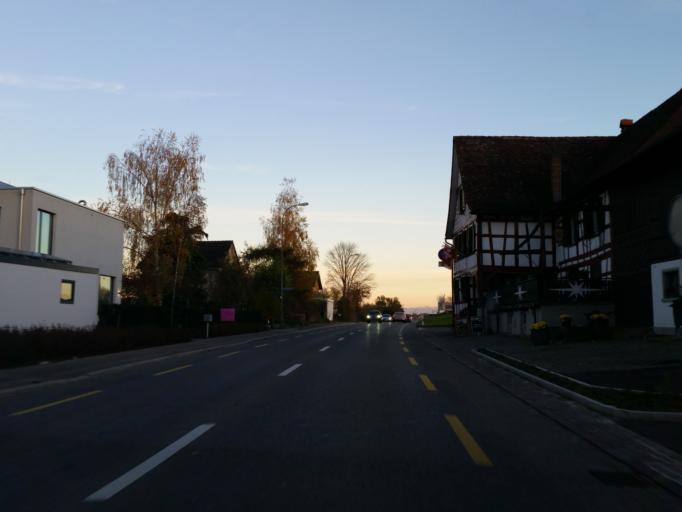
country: CH
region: Thurgau
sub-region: Kreuzlingen District
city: Munsterlingen
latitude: 47.6265
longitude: 9.2506
